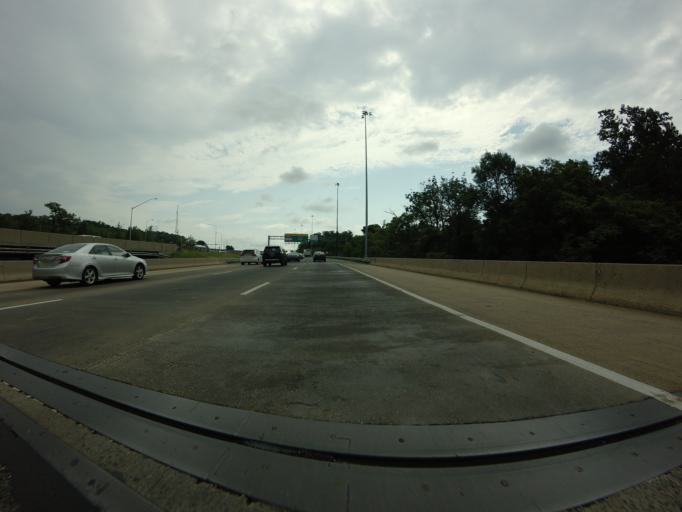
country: US
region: Maryland
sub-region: Cecil County
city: Perryville
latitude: 39.5855
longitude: -76.0804
